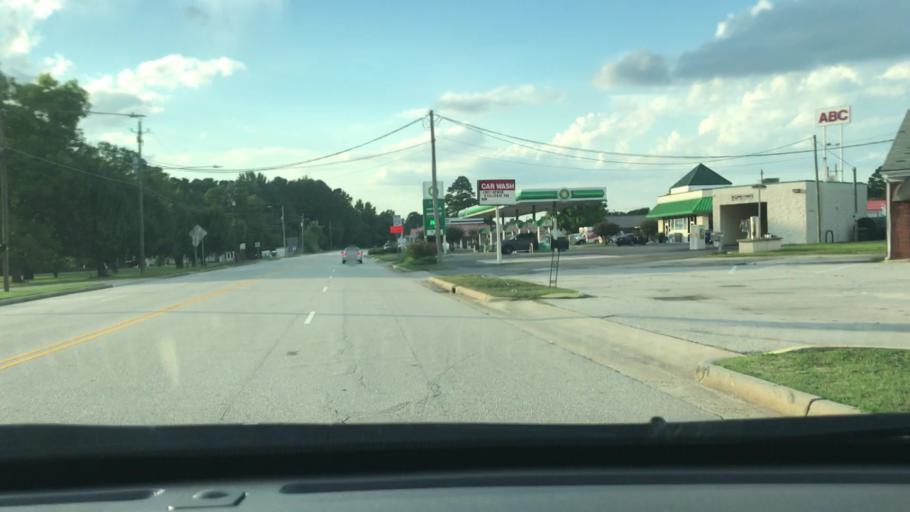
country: US
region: North Carolina
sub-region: Harnett County
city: Dunn
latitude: 35.2934
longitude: -78.6050
